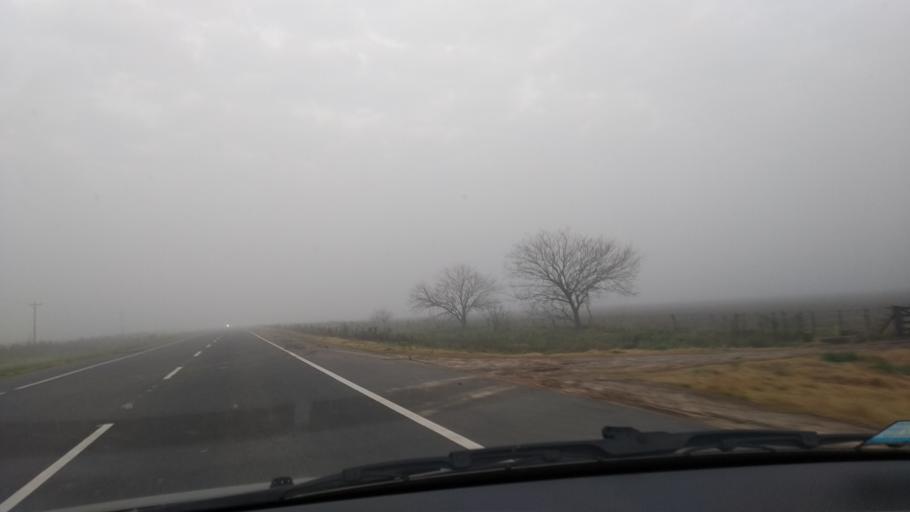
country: AR
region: Buenos Aires
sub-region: Partido de Brandsen
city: Brandsen
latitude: -35.2094
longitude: -58.4128
